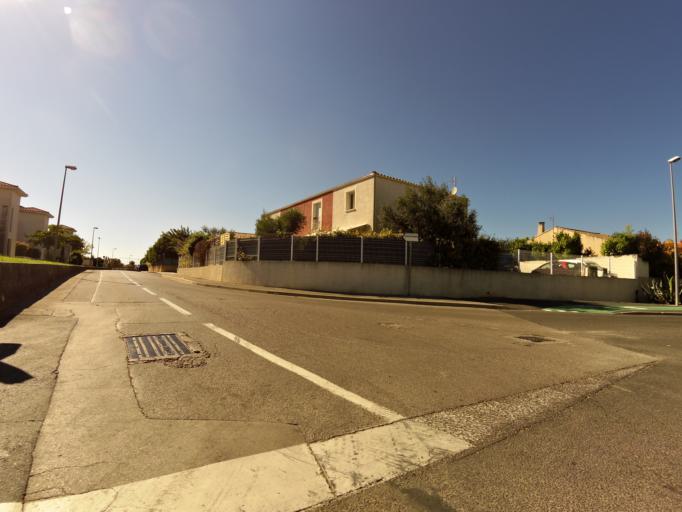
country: FR
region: Languedoc-Roussillon
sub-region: Departement de l'Herault
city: Lunel
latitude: 43.6664
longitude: 4.1332
